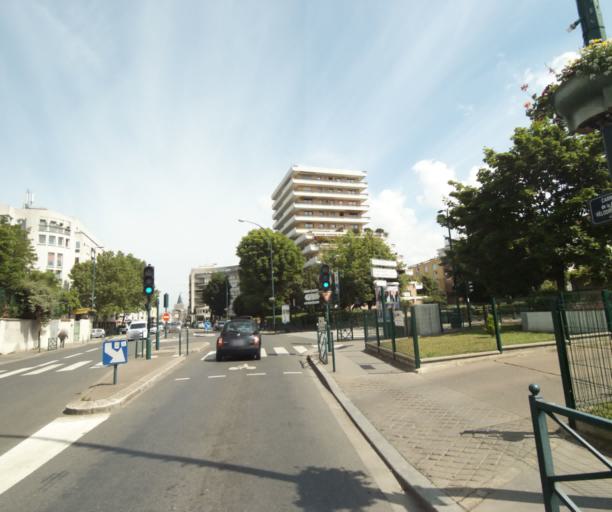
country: FR
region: Ile-de-France
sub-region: Departement des Hauts-de-Seine
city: Colombes
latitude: 48.9203
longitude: 2.2527
